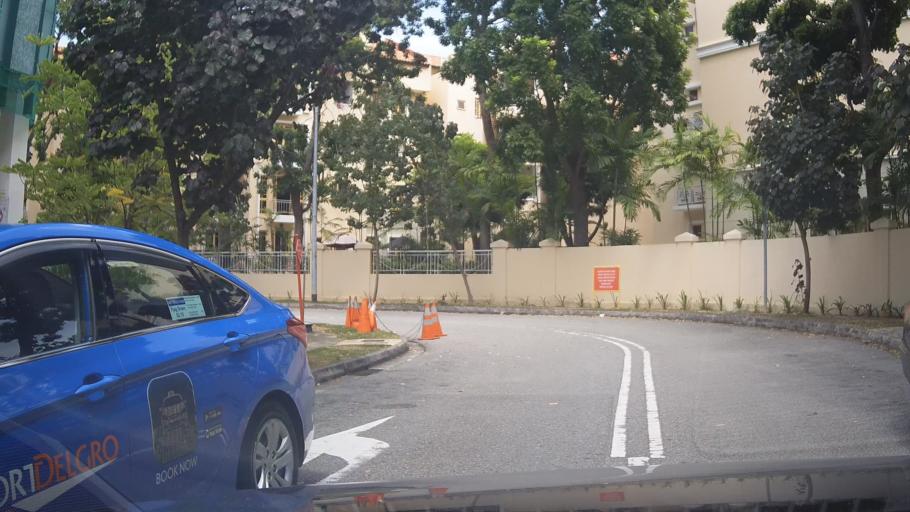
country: SG
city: Singapore
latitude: 1.3103
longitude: 103.9277
